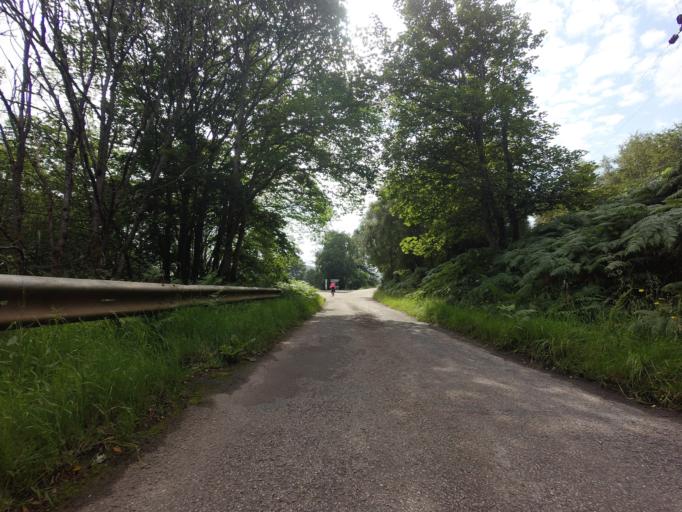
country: GB
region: Scotland
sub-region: Highland
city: Evanton
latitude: 57.9448
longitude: -4.4091
